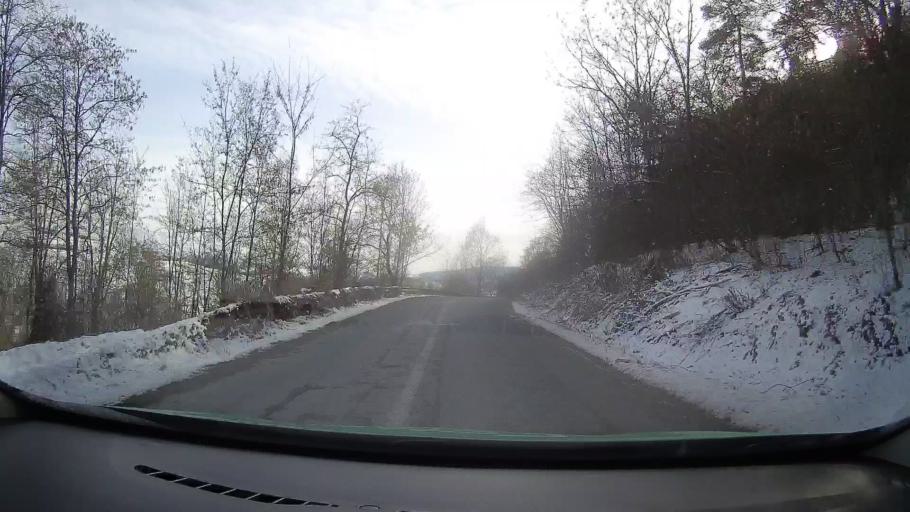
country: RO
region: Mures
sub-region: Comuna Apold
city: Saes
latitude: 46.1794
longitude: 24.7575
